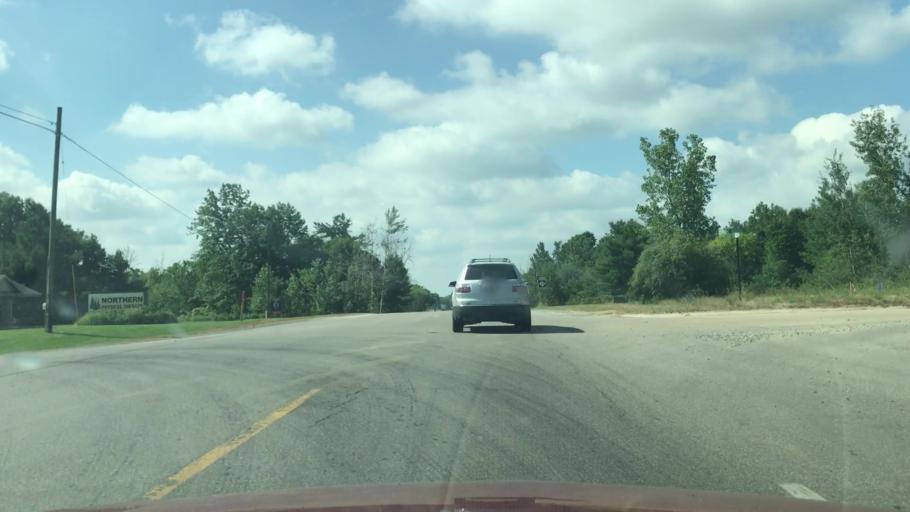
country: US
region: Michigan
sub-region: Kent County
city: Kent City
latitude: 43.2931
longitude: -85.8107
